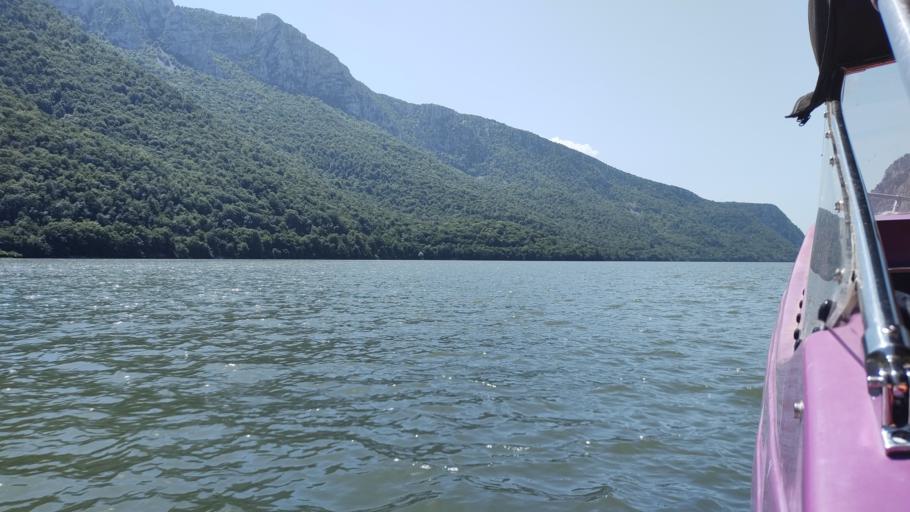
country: RO
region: Mehedinti
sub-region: Comuna Dubova
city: Dubova
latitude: 44.6094
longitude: 22.2705
